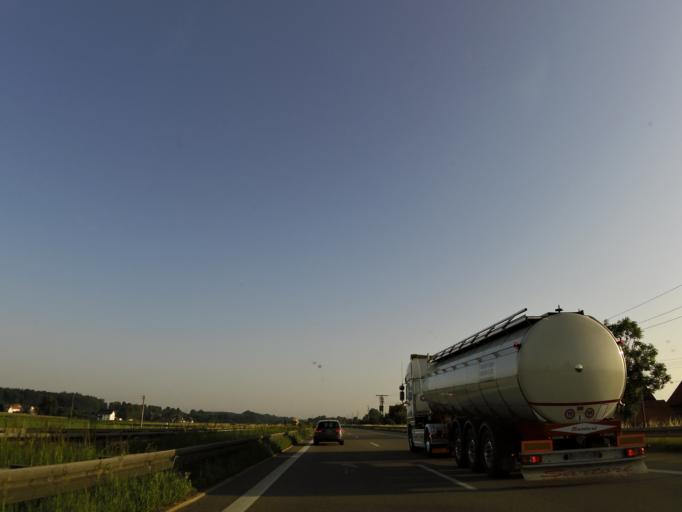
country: DE
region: Bavaria
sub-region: Swabia
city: Benningen
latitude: 47.9501
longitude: 10.1949
